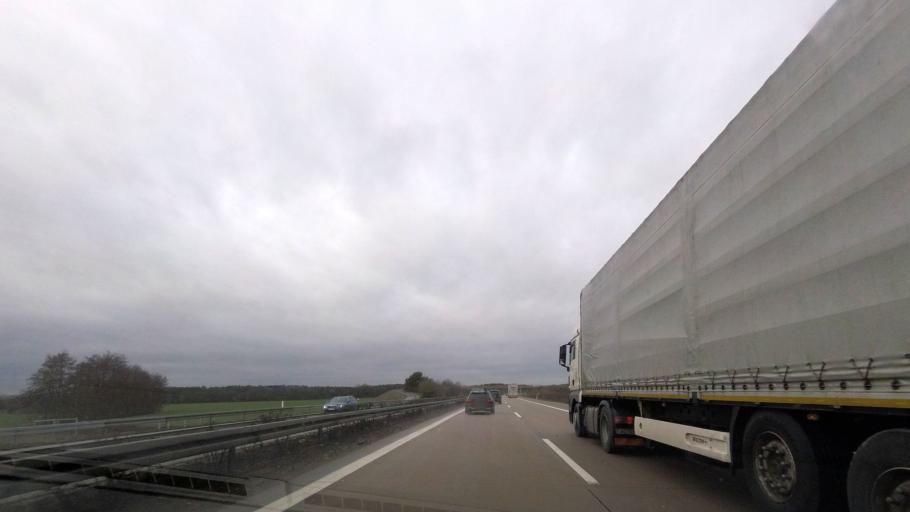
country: DE
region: Mecklenburg-Vorpommern
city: Rastow
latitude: 53.4346
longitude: 11.3983
